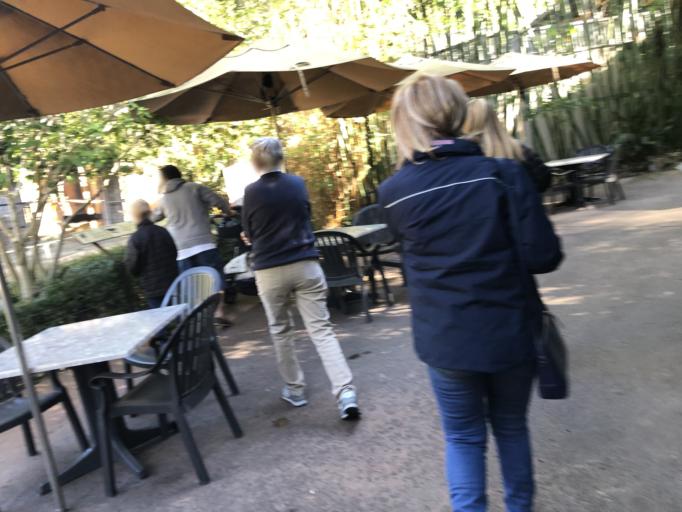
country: US
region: California
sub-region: San Diego County
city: San Diego
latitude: 32.7340
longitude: -117.1529
